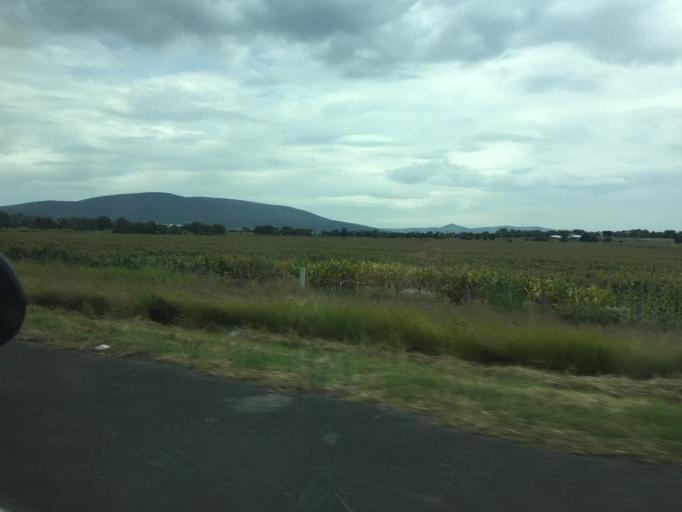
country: MX
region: Jalisco
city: Ocotlan
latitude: 20.3911
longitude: -102.7180
